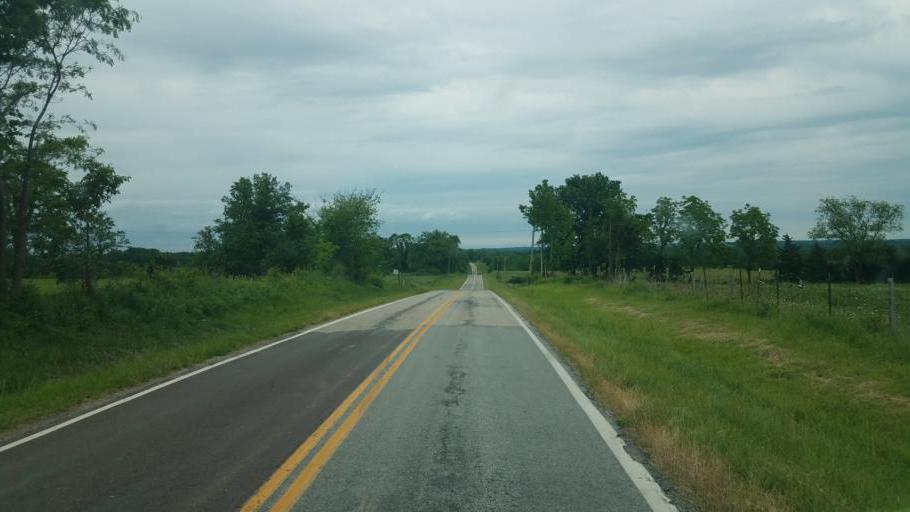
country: US
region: Missouri
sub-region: Moniteau County
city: California
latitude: 38.7098
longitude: -92.6344
